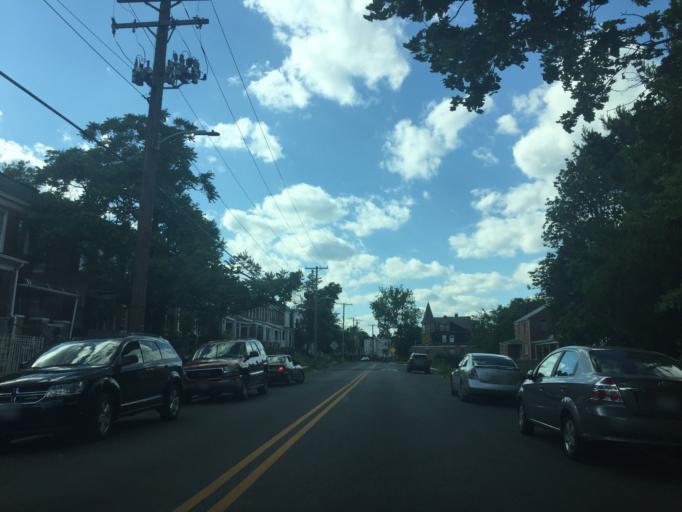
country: US
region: Maryland
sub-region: Baltimore County
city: Lochearn
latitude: 39.3430
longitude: -76.6672
